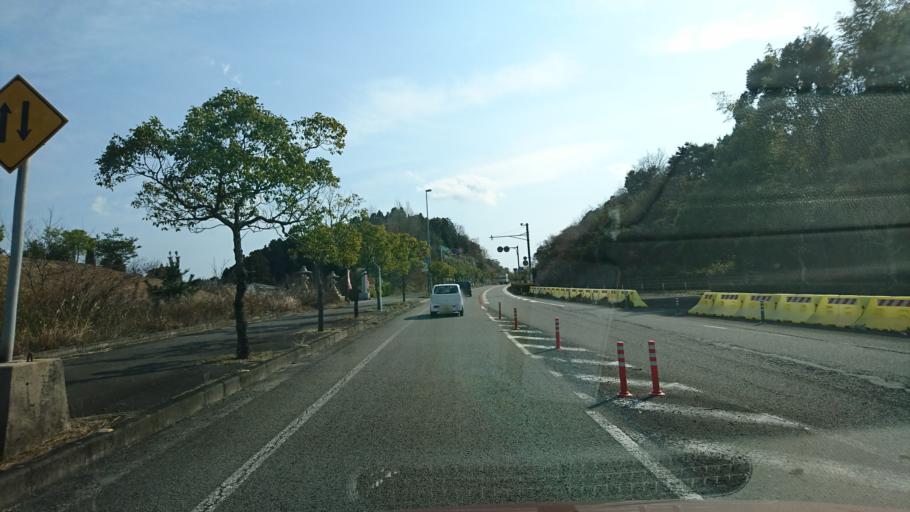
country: JP
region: Ehime
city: Saijo
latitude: 34.0166
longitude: 133.0319
